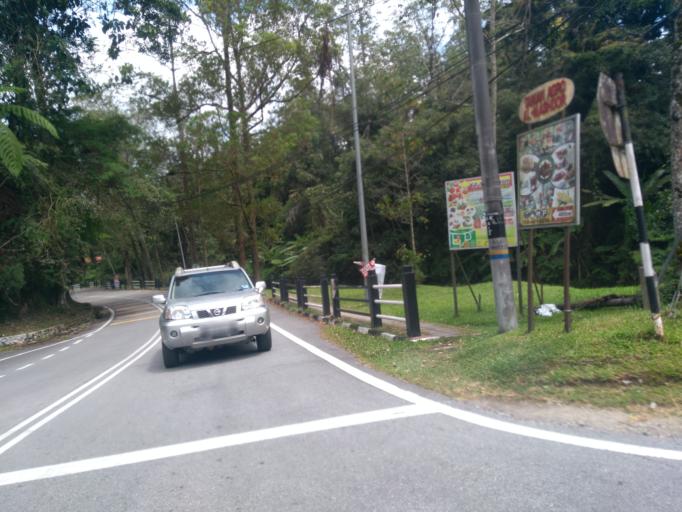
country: MY
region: Pahang
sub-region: Cameron Highlands
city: Tanah Rata
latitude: 4.4814
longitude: 101.3805
